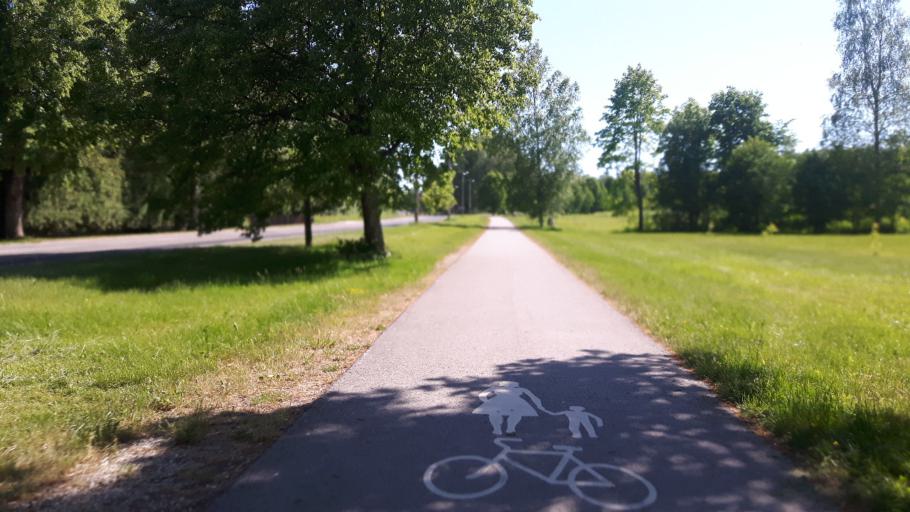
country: EE
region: Paernumaa
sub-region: Paikuse vald
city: Paikuse
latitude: 58.3965
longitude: 24.6411
